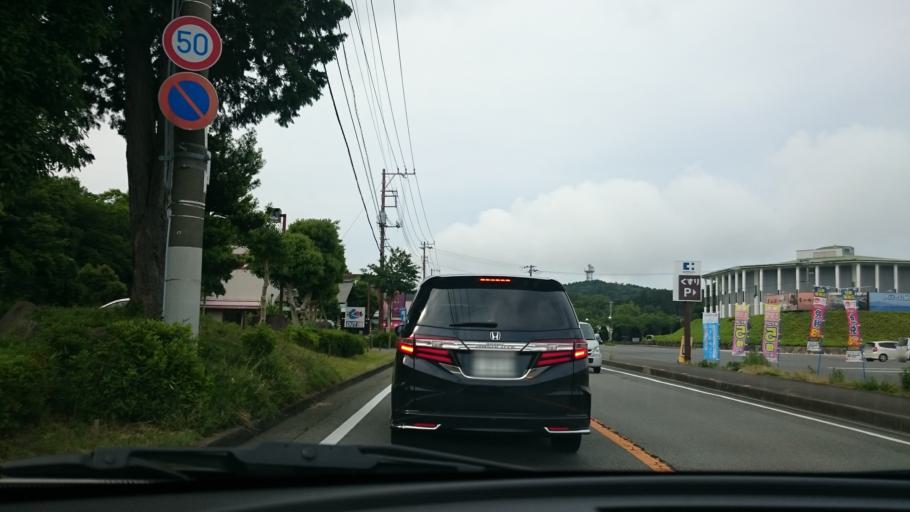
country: JP
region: Shizuoka
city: Ito
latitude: 34.9129
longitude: 139.1198
